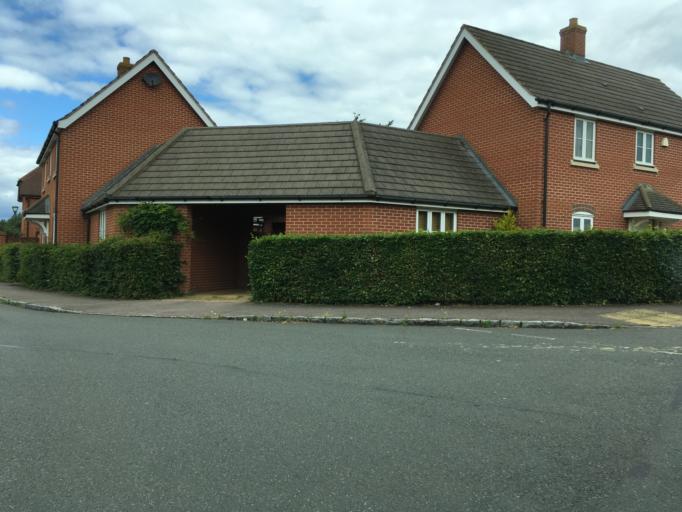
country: GB
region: England
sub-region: Milton Keynes
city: Simpson
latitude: 52.0323
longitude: -0.7117
